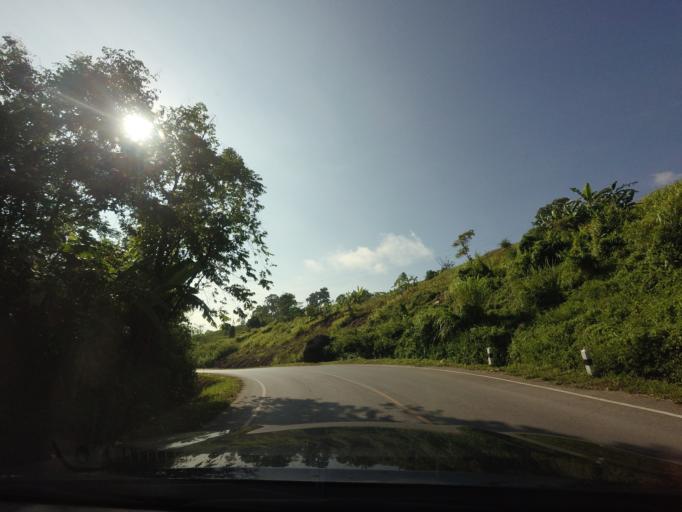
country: TH
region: Phetchabun
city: Lom Kao
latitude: 16.8829
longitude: 101.1156
